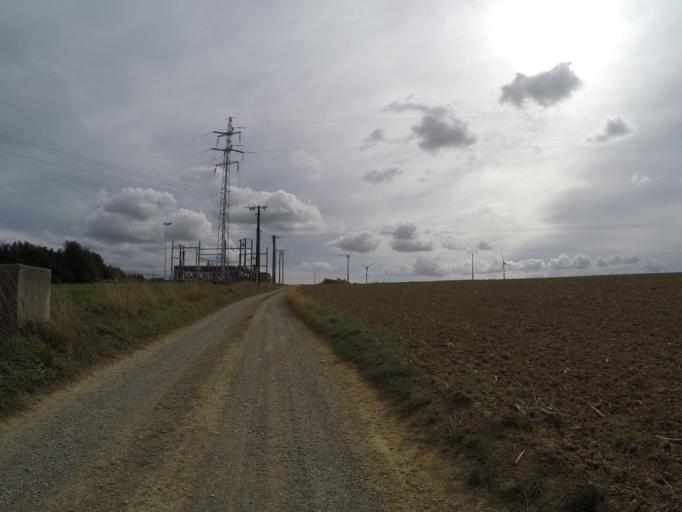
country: BE
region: Wallonia
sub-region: Province de Namur
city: Assesse
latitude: 50.3070
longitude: 4.9797
